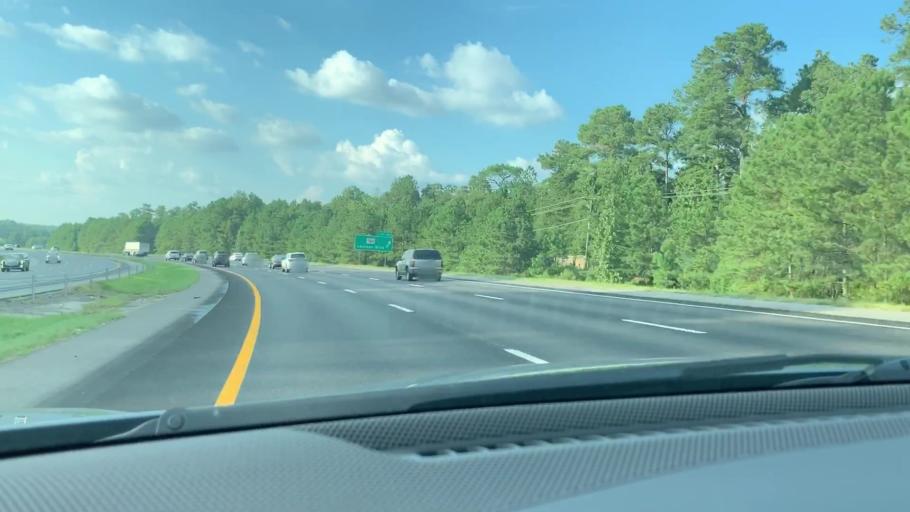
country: US
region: South Carolina
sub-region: Richland County
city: Forest Acres
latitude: 33.9897
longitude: -80.9531
